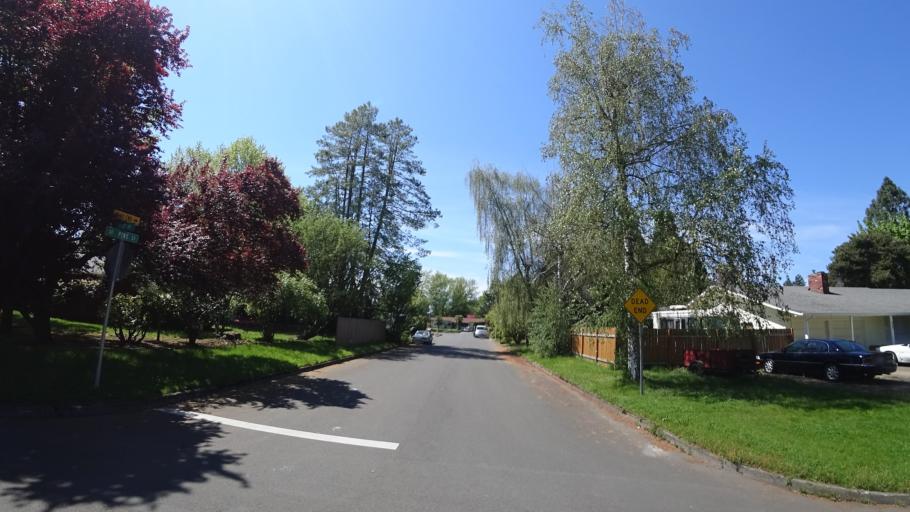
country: US
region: Oregon
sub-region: Washington County
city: Hillsboro
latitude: 45.5125
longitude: -122.9641
